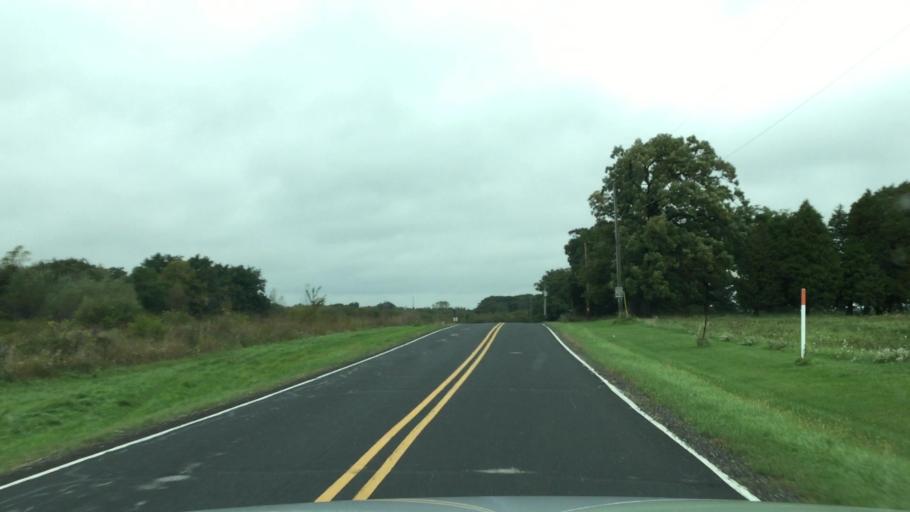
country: US
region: Wisconsin
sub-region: Racine County
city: Waterford
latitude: 42.7607
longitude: -88.1657
